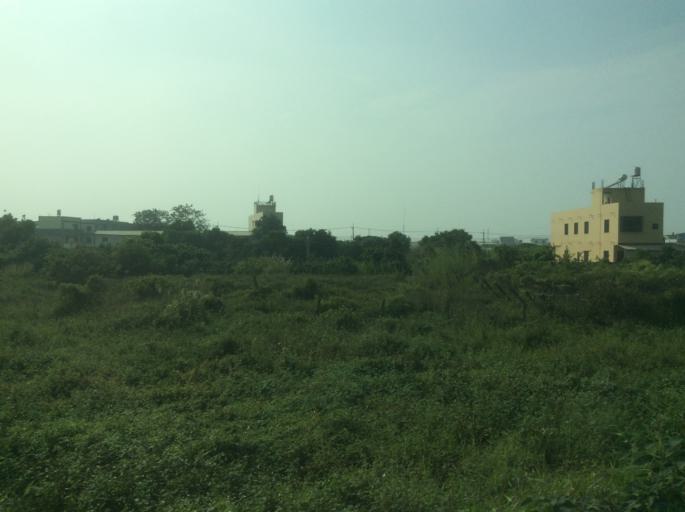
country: TW
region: Taiwan
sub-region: Changhua
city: Chang-hua
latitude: 23.9817
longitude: 120.5638
